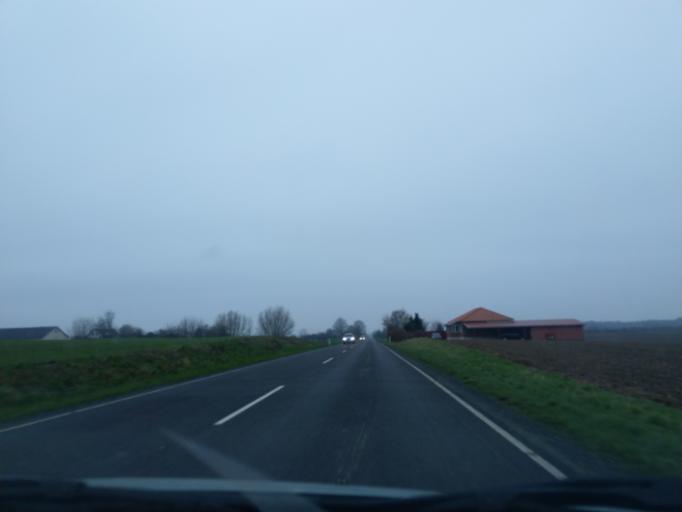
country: DK
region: Zealand
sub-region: Vordingborg Kommune
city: Praesto
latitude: 55.1183
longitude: 12.0143
